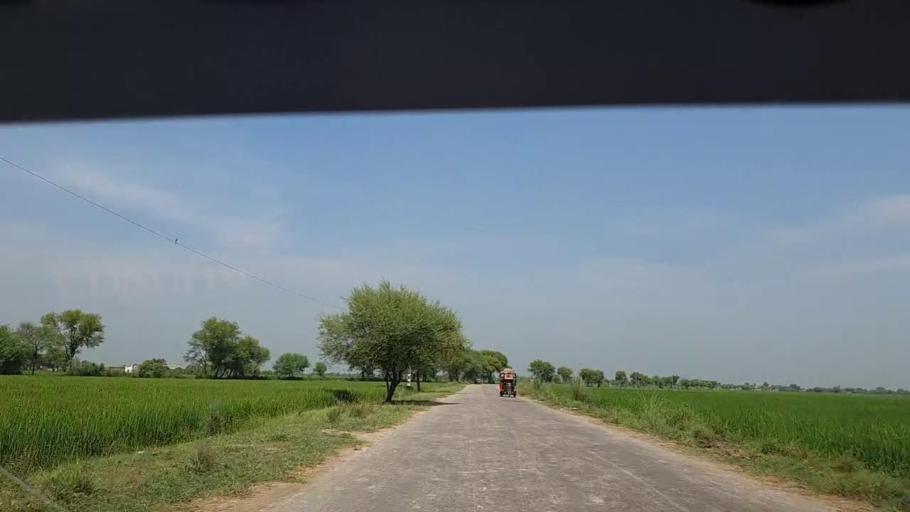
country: PK
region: Sindh
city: Thul
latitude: 28.1391
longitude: 68.7160
